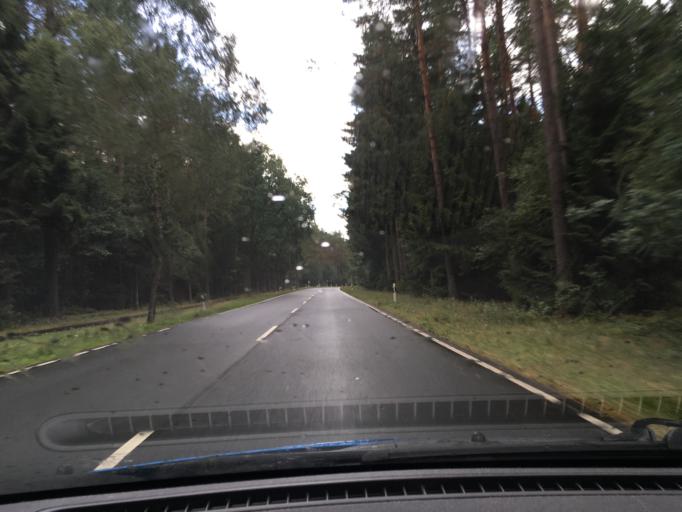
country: DE
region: Lower Saxony
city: Wietzendorf
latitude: 52.9737
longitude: 9.9507
